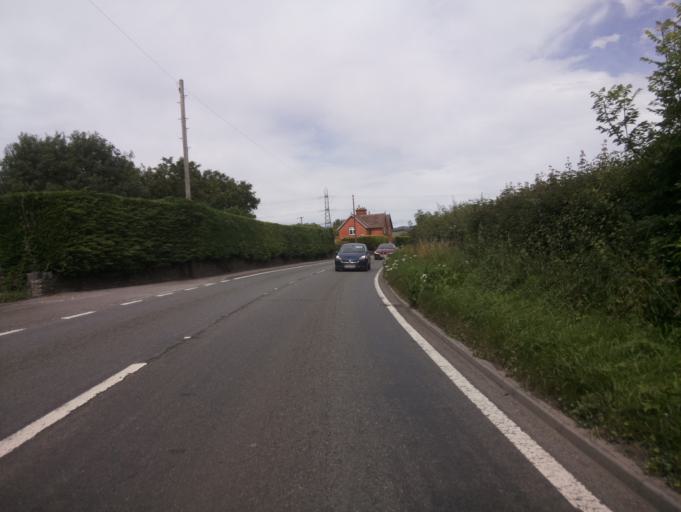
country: GB
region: England
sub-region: Somerset
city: Glastonbury
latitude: 51.1831
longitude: -2.6911
